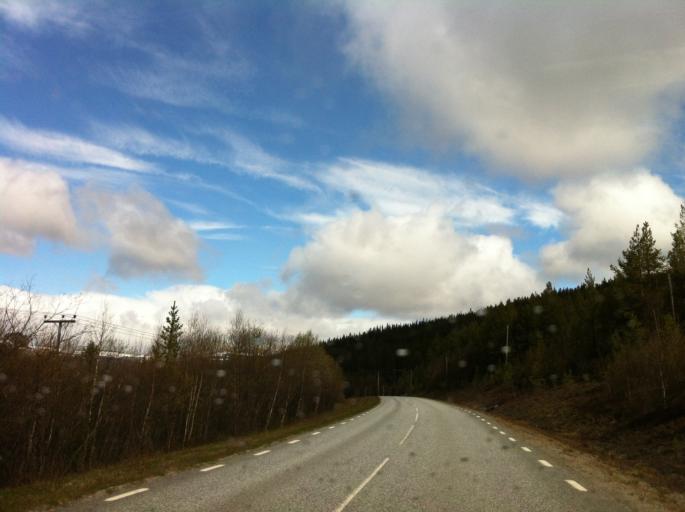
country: SE
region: Jaemtland
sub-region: Are Kommun
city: Are
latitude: 62.5800
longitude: 12.5592
